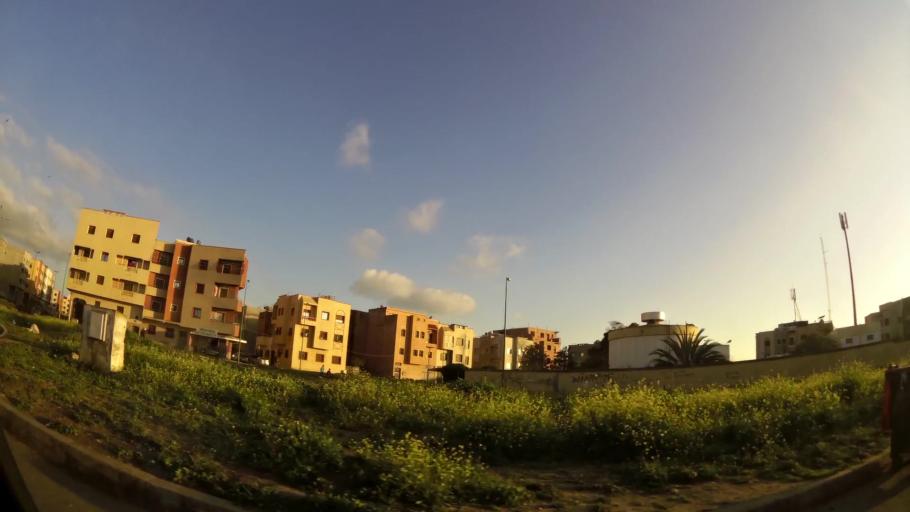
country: MA
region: Chaouia-Ouardigha
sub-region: Settat Province
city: Settat
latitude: 32.9910
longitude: -7.6009
